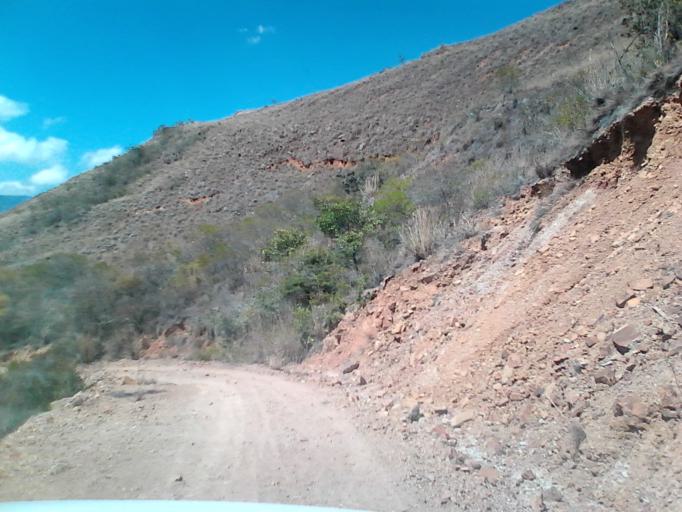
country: CO
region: Boyaca
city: Villa de Leiva
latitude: 5.6134
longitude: -73.5738
